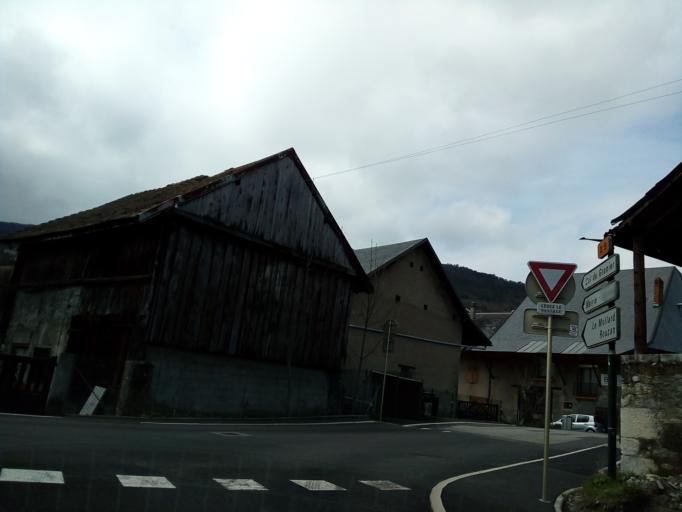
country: FR
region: Rhone-Alpes
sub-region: Departement de la Savoie
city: Saint-Baldoph
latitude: 45.5350
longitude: 5.9535
